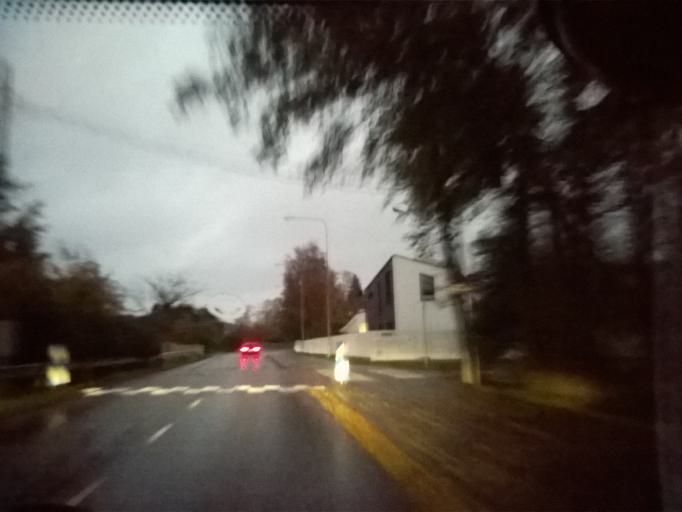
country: EE
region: Harju
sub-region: Viimsi vald
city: Haabneeme
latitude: 59.5160
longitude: 24.8169
